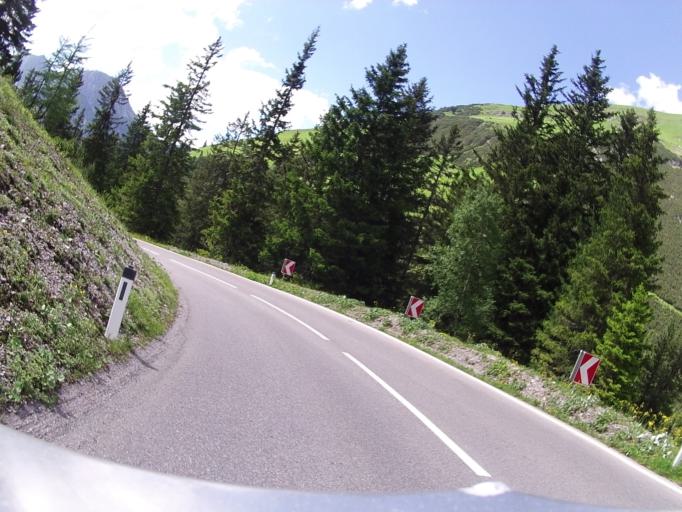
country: AT
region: Tyrol
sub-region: Politischer Bezirk Reutte
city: Namlos
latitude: 47.2834
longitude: 10.6326
